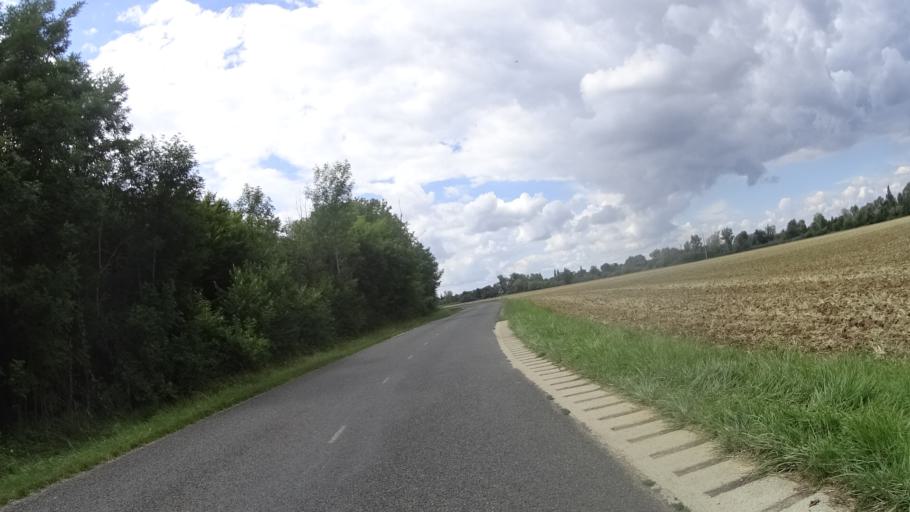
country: FR
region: Champagne-Ardenne
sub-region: Departement de la Haute-Marne
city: Villiers-en-Lieu
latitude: 48.6462
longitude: 4.8364
